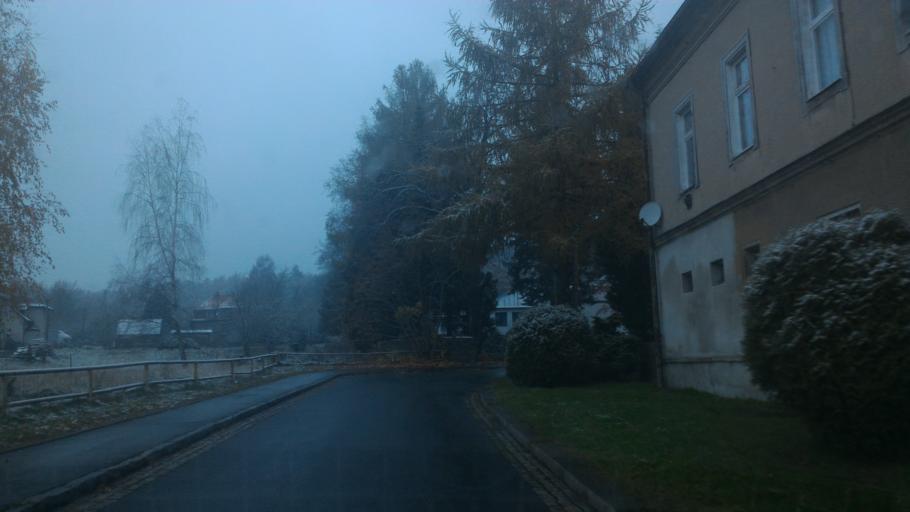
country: CZ
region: Ustecky
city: Jirikov
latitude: 51.0020
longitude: 14.5749
